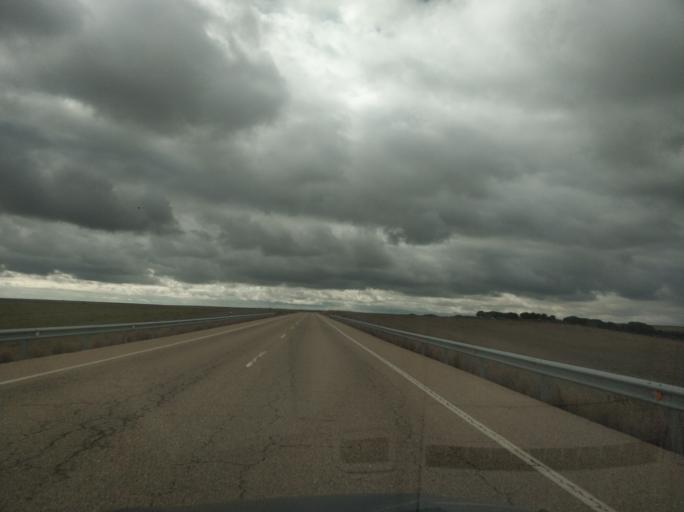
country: ES
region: Castille and Leon
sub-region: Provincia de Valladolid
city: Alaejos
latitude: 41.2729
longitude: -5.2553
